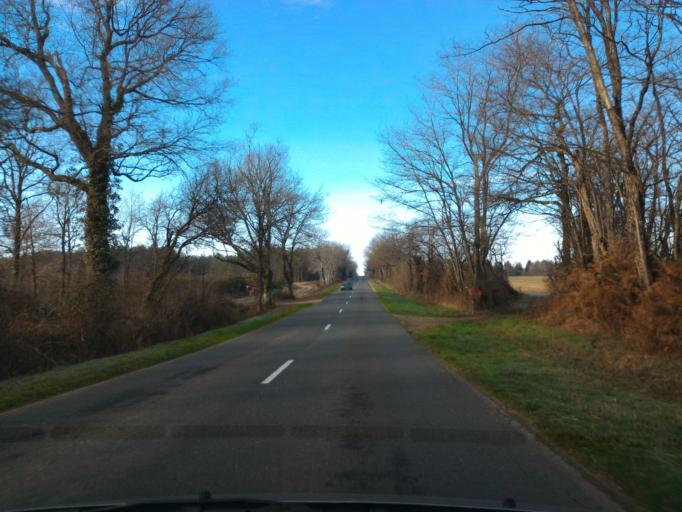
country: FR
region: Poitou-Charentes
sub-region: Departement de la Charente
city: Confolens
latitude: 46.0336
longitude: 0.5957
